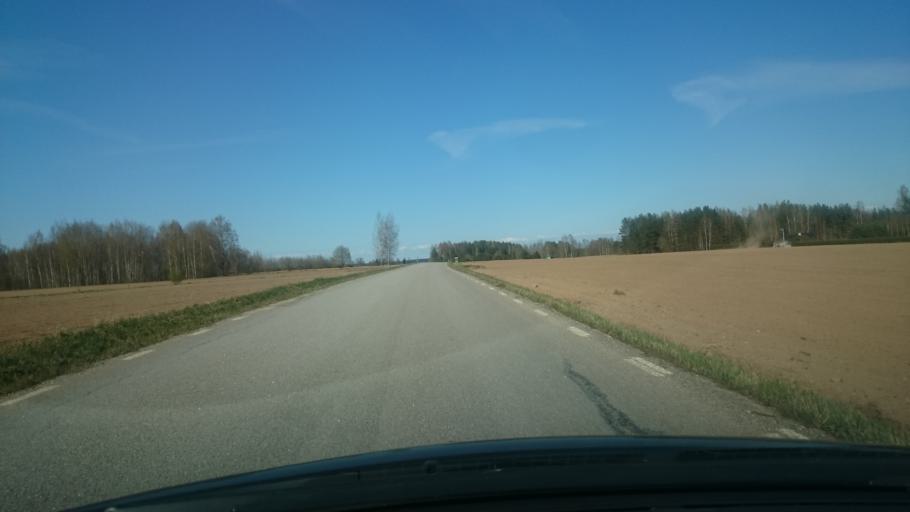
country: EE
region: Polvamaa
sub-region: Polva linn
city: Polva
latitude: 58.1765
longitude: 27.0809
